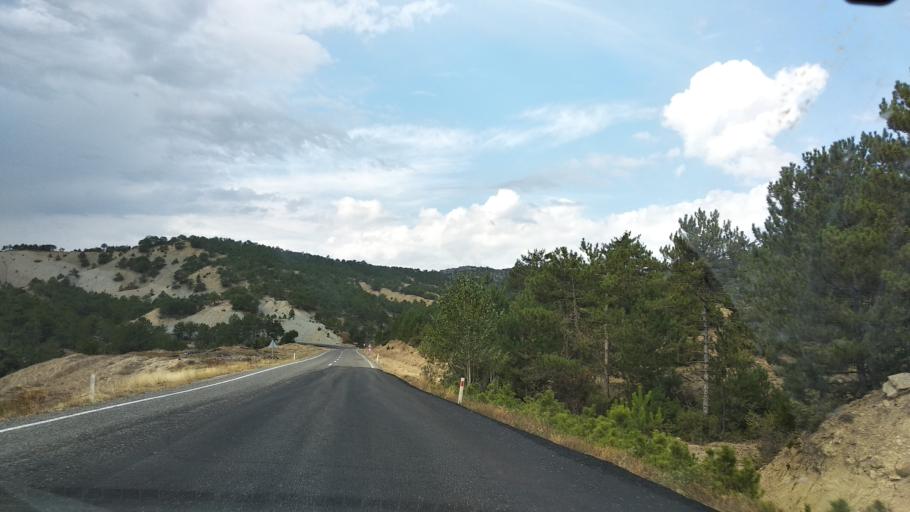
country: TR
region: Bolu
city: Seben
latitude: 40.3589
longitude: 31.4854
